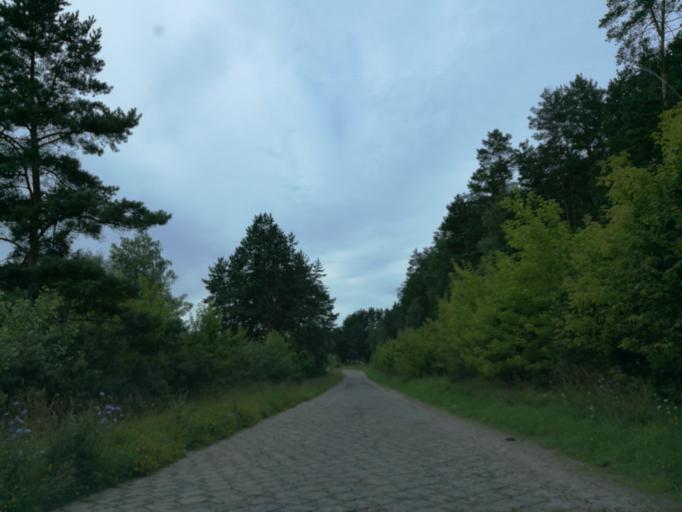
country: LT
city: Grigiskes
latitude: 54.6896
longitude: 25.0474
